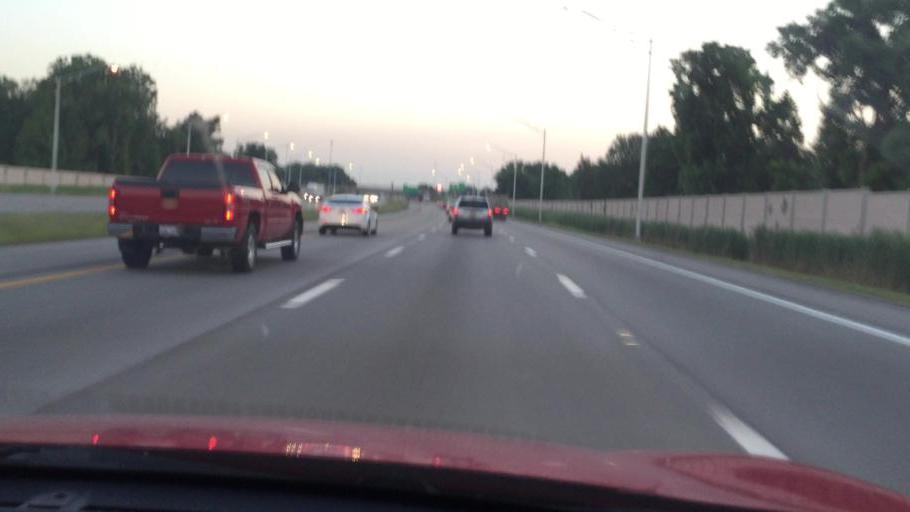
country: US
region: Ohio
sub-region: Lucas County
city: Holland
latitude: 41.6683
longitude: -83.6934
